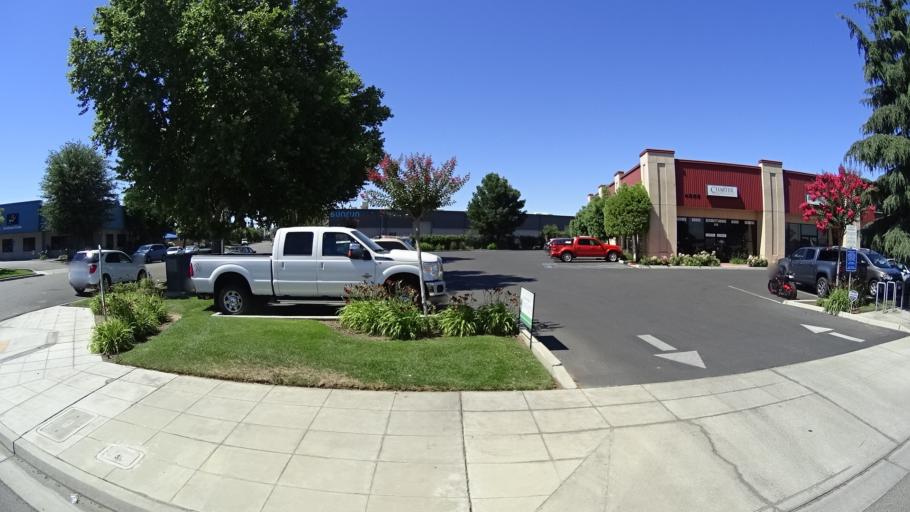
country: US
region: California
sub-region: Fresno County
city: West Park
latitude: 36.8028
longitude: -119.8568
